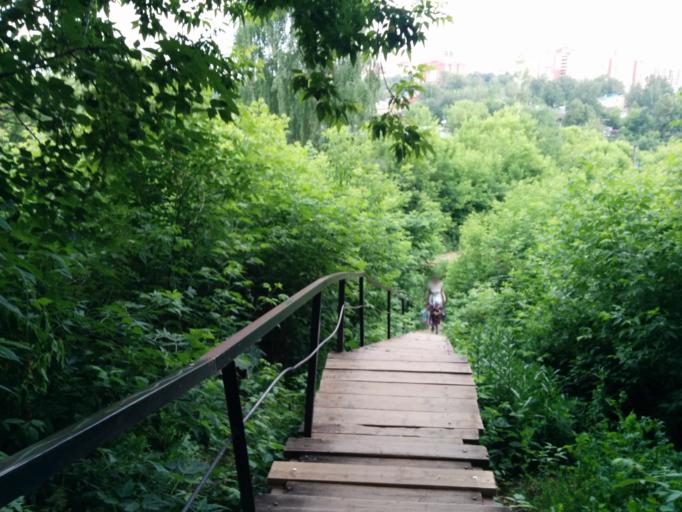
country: RU
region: Perm
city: Perm
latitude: 58.0204
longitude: 56.2657
